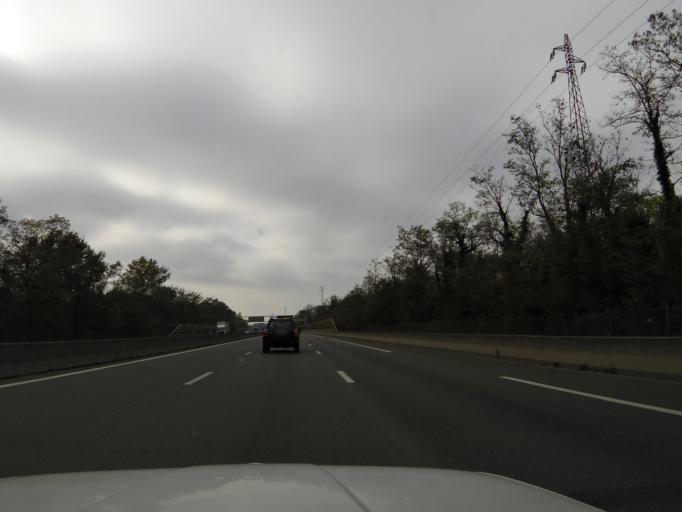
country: FR
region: Rhone-Alpes
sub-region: Departement de l'Ain
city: Miribel
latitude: 45.8144
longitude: 4.9529
